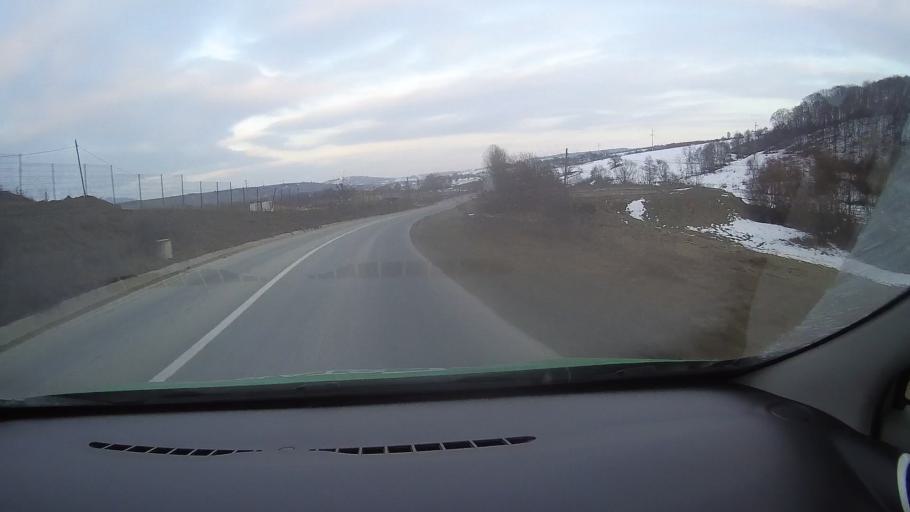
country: RO
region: Harghita
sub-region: Comuna Lupeni
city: Lupeni
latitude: 46.3579
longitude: 25.1963
